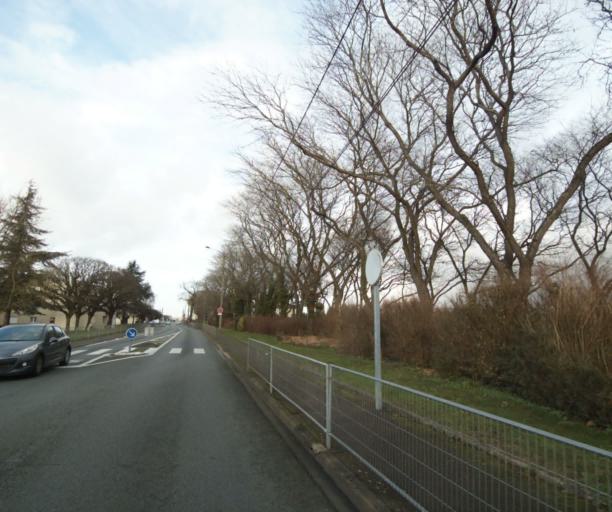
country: FR
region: Pays de la Loire
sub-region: Departement de la Sarthe
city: Le Mans
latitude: 47.9634
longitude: 0.2091
